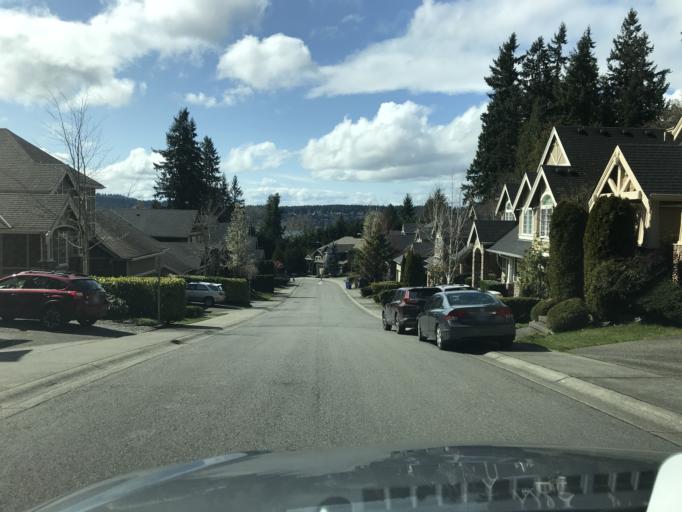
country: US
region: Washington
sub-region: King County
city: West Lake Sammamish
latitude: 47.5852
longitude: -122.0789
